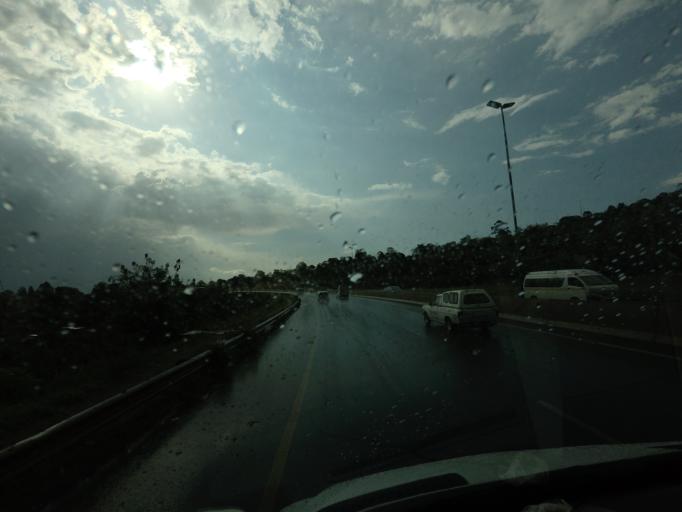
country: SZ
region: Manzini
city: Kwaluseni
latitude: -26.4892
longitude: 31.3469
